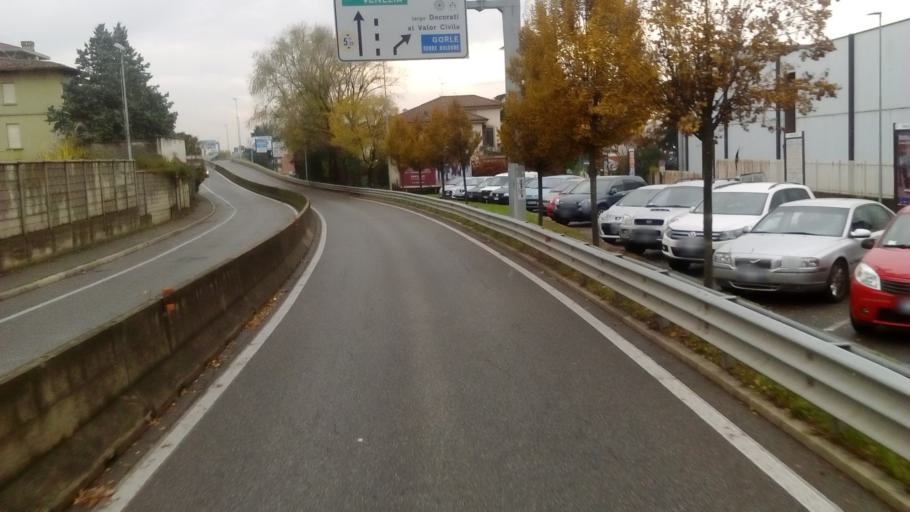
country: IT
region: Lombardy
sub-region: Provincia di Bergamo
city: Torre Boldone
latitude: 45.7096
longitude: 9.6895
